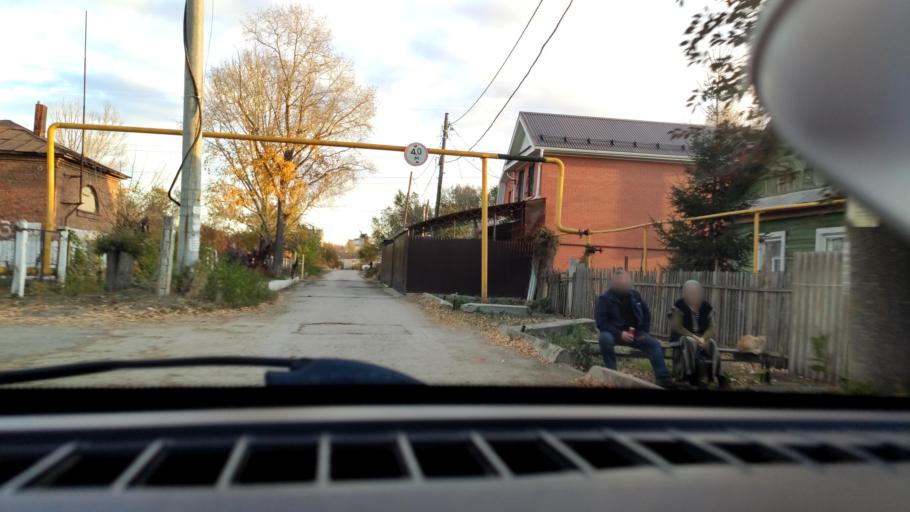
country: RU
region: Samara
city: Smyshlyayevka
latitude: 53.2302
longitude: 50.3057
